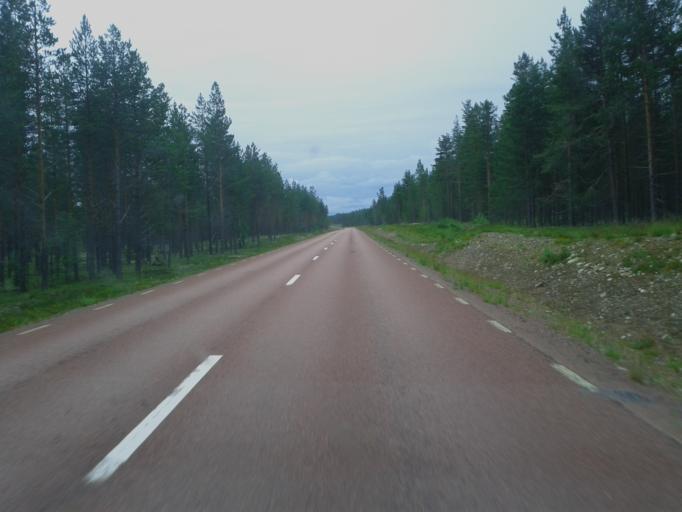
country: NO
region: Hedmark
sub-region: Trysil
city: Innbygda
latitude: 61.6812
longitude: 13.1653
